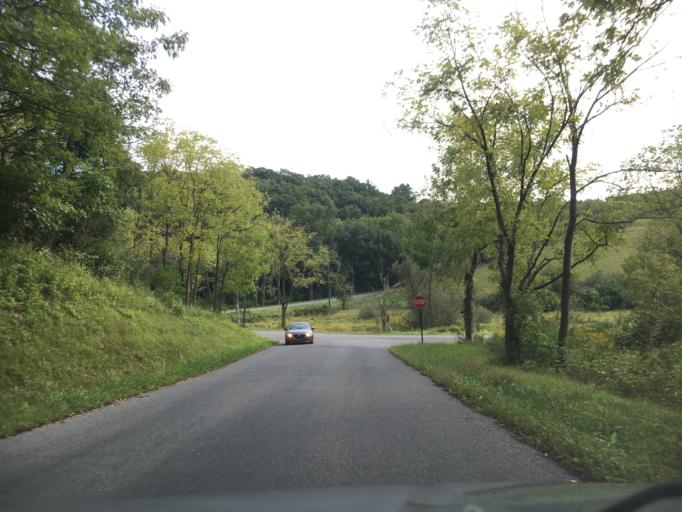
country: US
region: Pennsylvania
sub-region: Berks County
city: Topton
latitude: 40.6089
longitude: -75.7154
